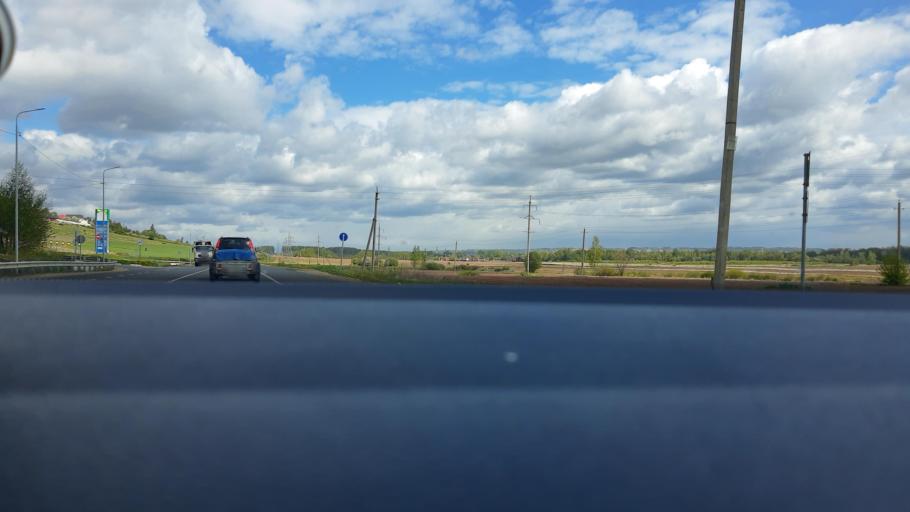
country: RU
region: Moskovskaya
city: Yakhroma
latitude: 56.3368
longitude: 37.4822
